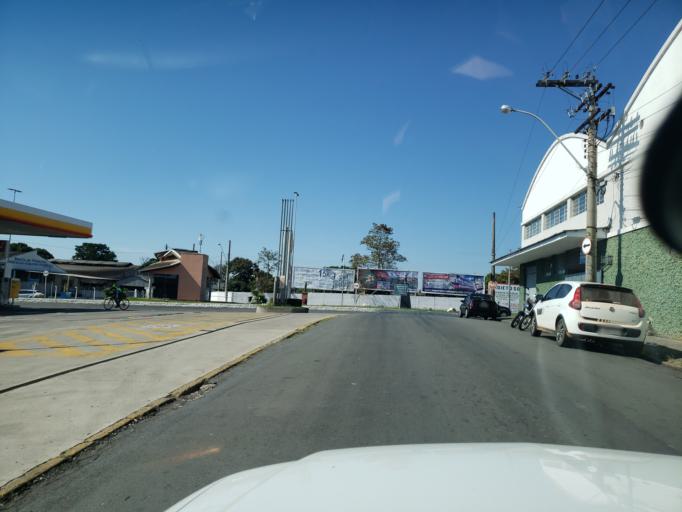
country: BR
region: Sao Paulo
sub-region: Itapira
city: Itapira
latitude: -22.4440
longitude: -46.8316
